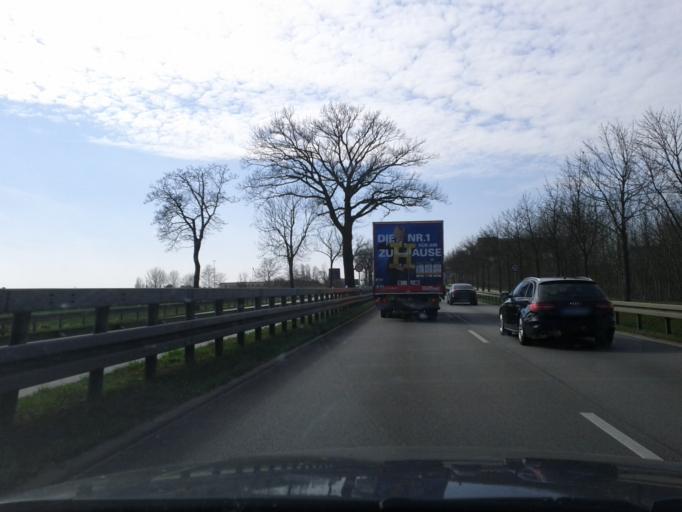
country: DE
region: Berlin
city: Mahlsdorf
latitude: 52.5030
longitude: 13.6310
